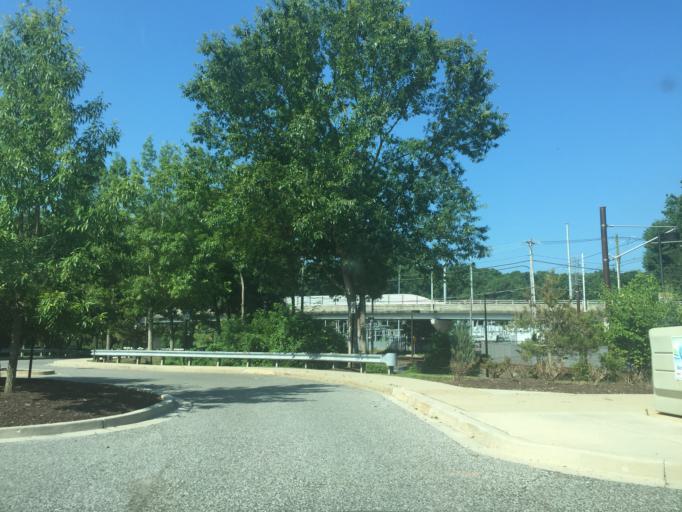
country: US
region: Maryland
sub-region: Baltimore County
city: Lutherville
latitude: 39.3763
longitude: -76.6499
